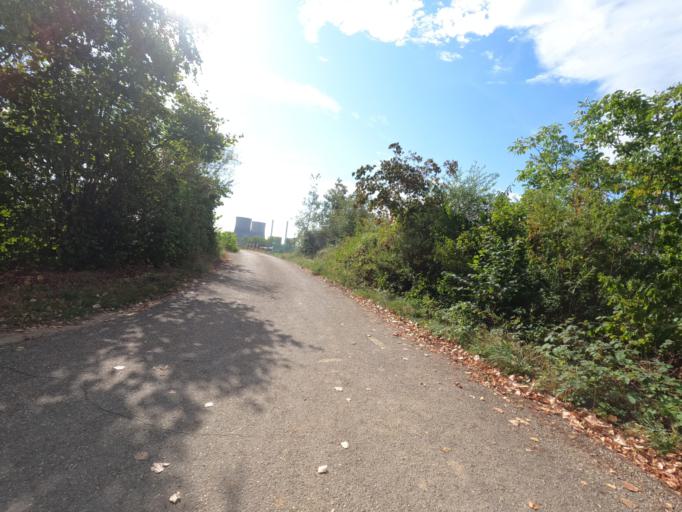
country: NL
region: Limburg
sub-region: Gemeente Maasgouw
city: Maasbracht
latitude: 51.1662
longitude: 5.8932
